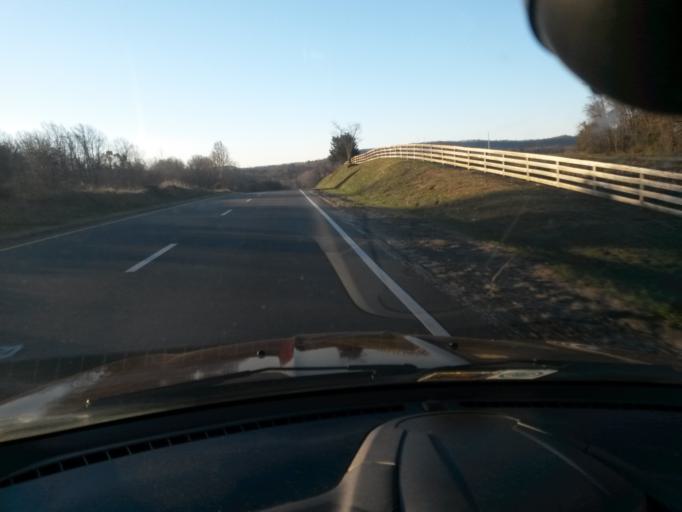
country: US
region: Virginia
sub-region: Franklin County
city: Henry Fork
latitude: 36.9387
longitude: -79.8738
